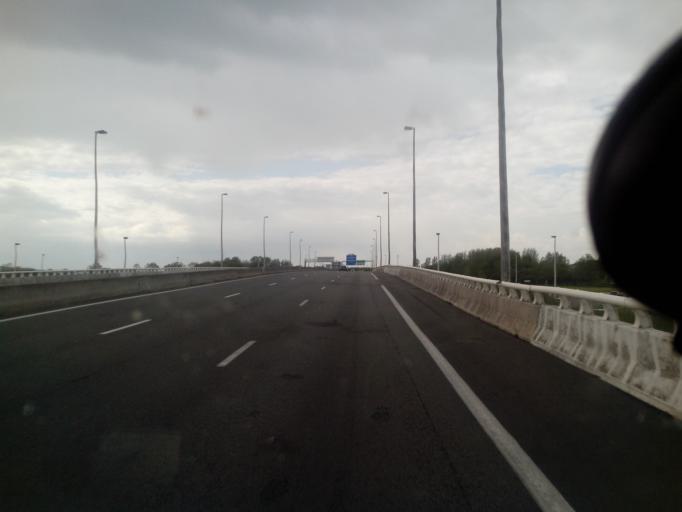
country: FR
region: Nord-Pas-de-Calais
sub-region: Departement du Pas-de-Calais
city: Calais
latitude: 50.9386
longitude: 1.8391
